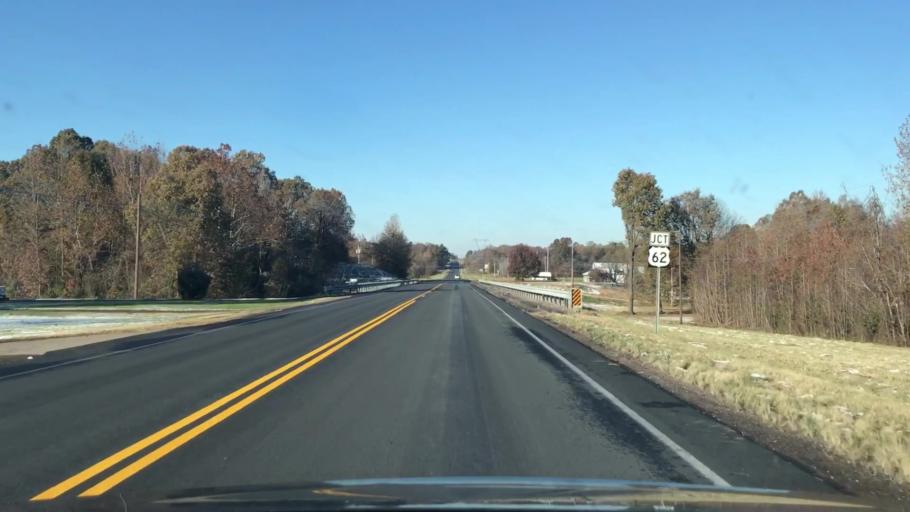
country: US
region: Kentucky
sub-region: Marshall County
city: Calvert City
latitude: 37.0053
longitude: -88.4019
